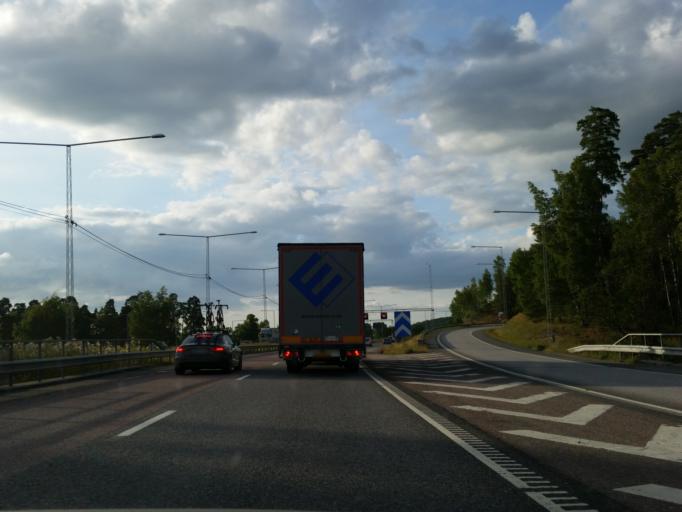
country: SE
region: Stockholm
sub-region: Sodertalje Kommun
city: Pershagen
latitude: 59.1775
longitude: 17.6431
